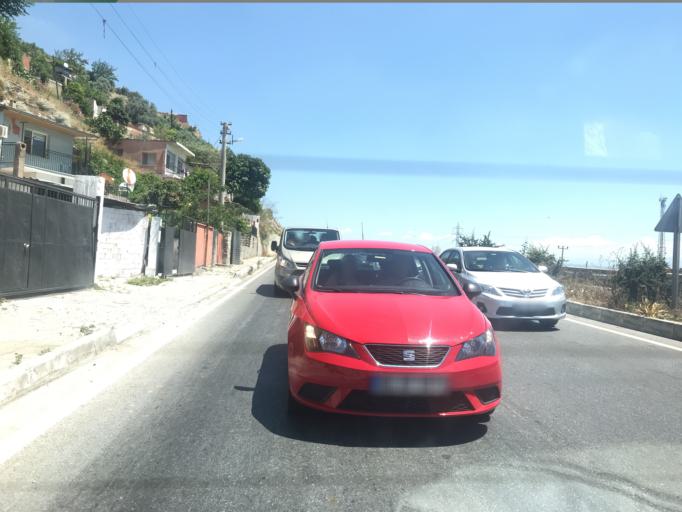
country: TR
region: Aydin
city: Soeke
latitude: 37.7857
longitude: 27.4647
